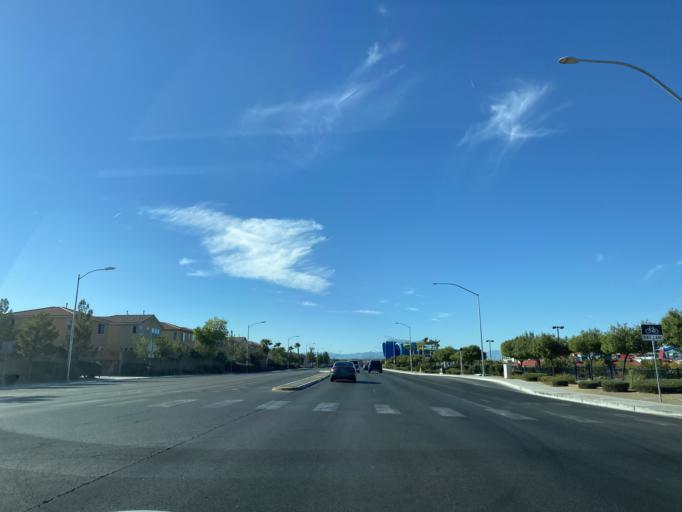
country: US
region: Nevada
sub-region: Clark County
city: Henderson
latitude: 36.0710
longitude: -115.0220
